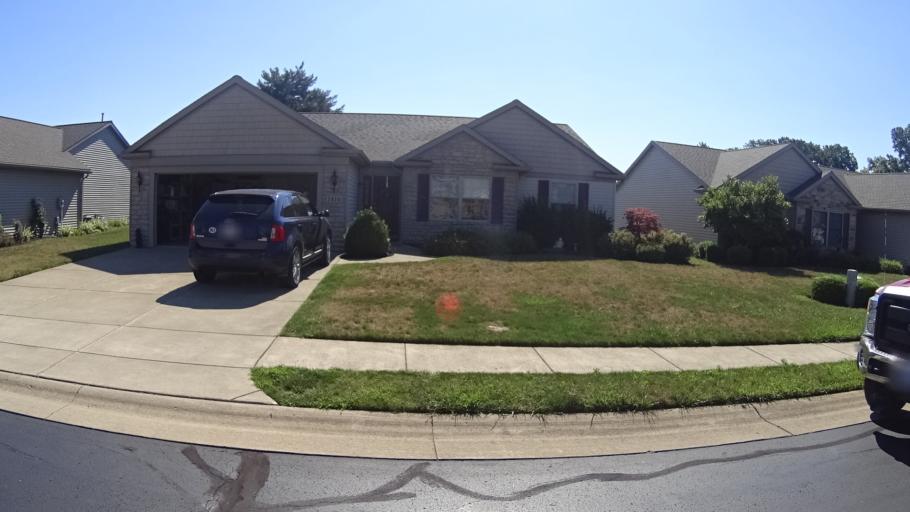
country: US
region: Ohio
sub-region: Erie County
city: Huron
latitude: 41.3909
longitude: -82.6418
